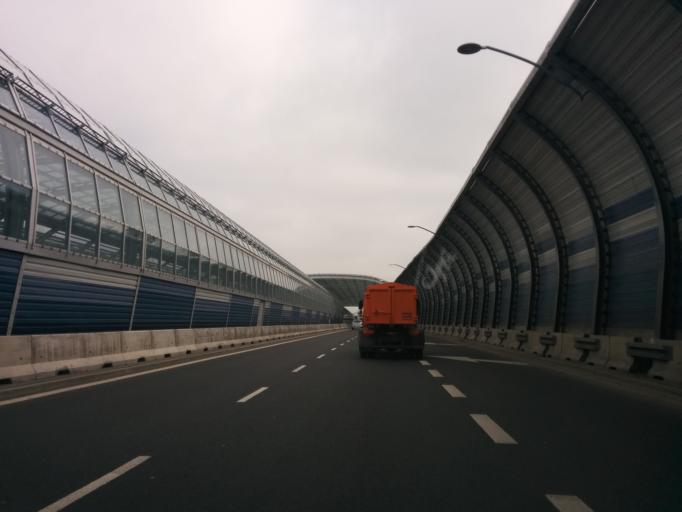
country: PL
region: Masovian Voivodeship
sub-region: Warszawa
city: Targowek
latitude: 52.2950
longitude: 21.0181
